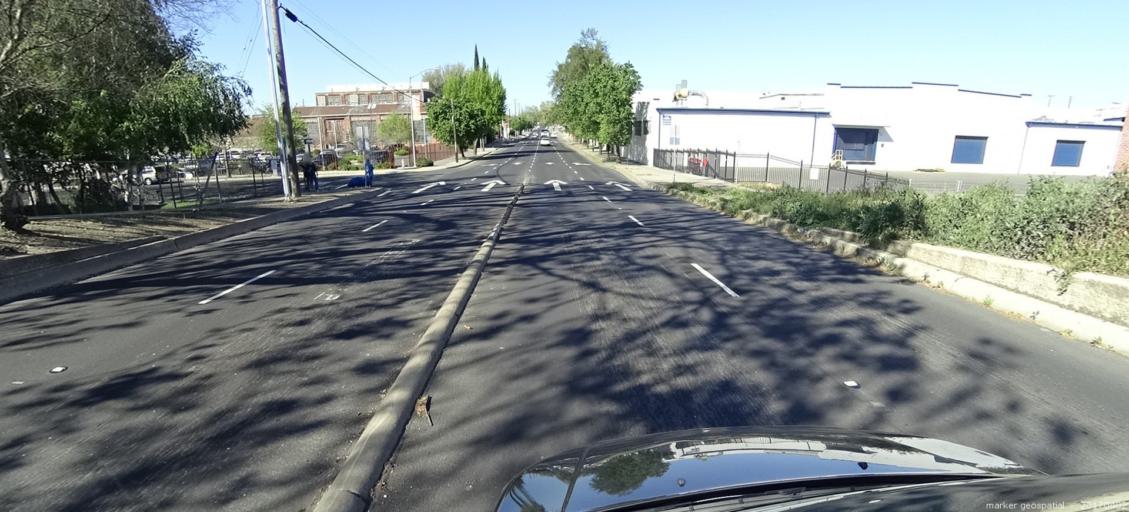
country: US
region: California
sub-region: Sacramento County
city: Sacramento
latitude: 38.5875
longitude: -121.4812
